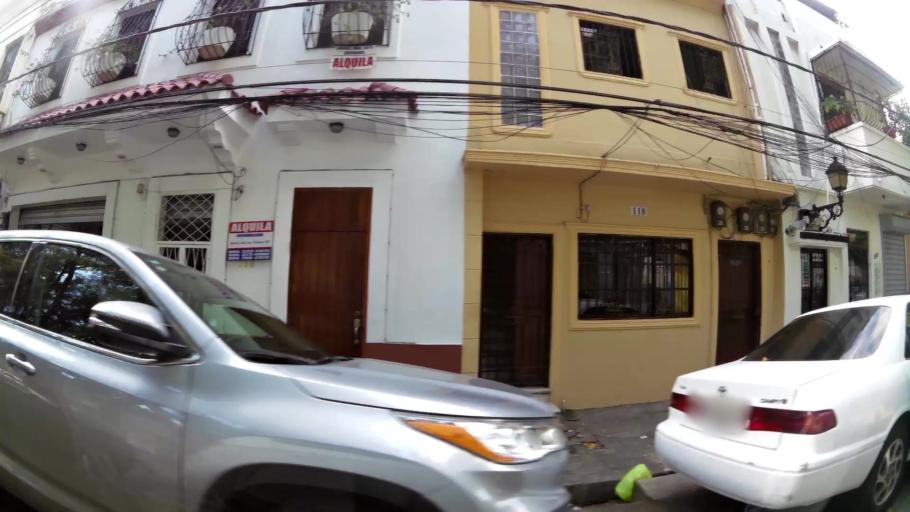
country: DO
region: Nacional
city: Ciudad Nueva
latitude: 18.4701
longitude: -69.8854
